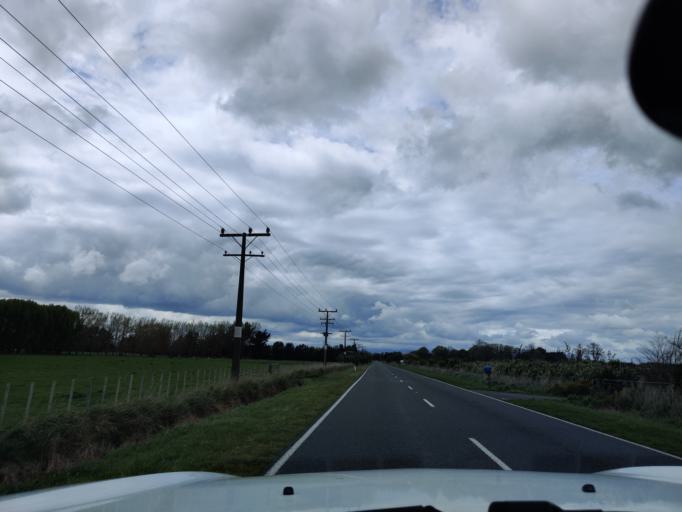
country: NZ
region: Manawatu-Wanganui
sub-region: Palmerston North City
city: Palmerston North
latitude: -40.2459
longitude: 175.5456
